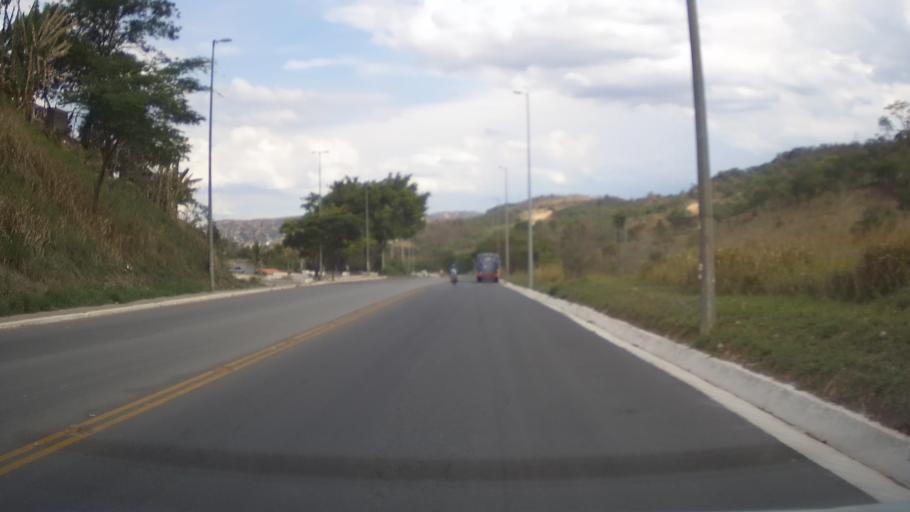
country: BR
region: Minas Gerais
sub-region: Belo Horizonte
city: Belo Horizonte
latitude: -19.8694
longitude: -43.8914
